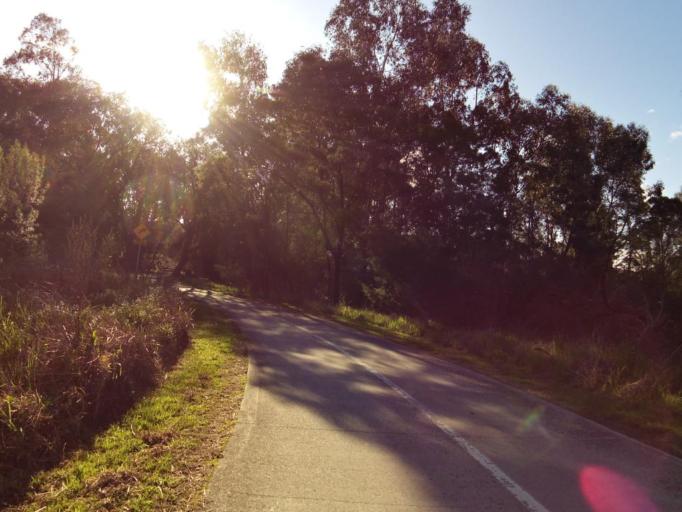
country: AU
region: Victoria
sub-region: Knox
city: Wantirna
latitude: -37.8470
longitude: 145.2123
